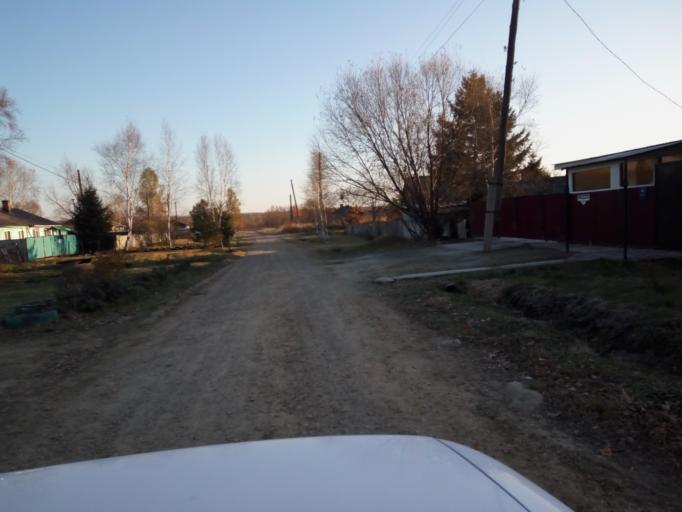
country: RU
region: Primorskiy
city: Lazo
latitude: 45.8808
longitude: 133.6537
